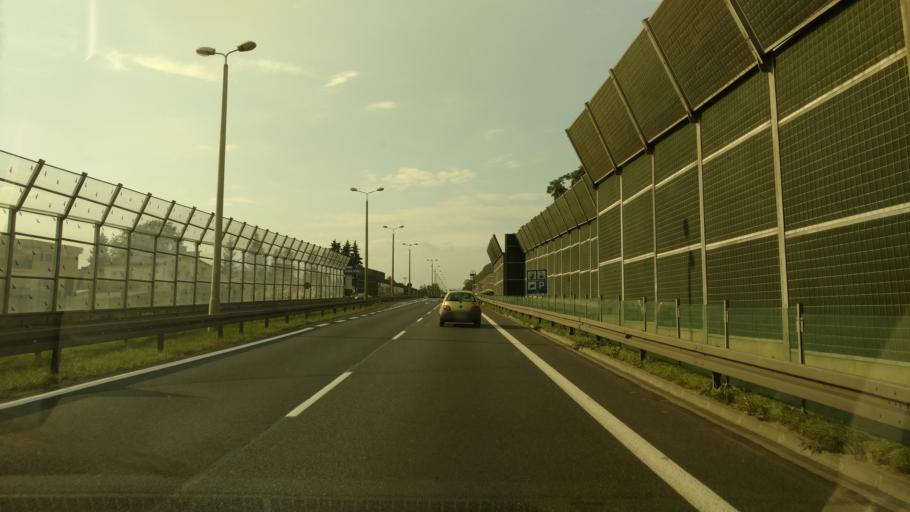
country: PL
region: Silesian Voivodeship
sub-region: Powiat pszczynski
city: Pszczyna
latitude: 49.9829
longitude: 18.9573
